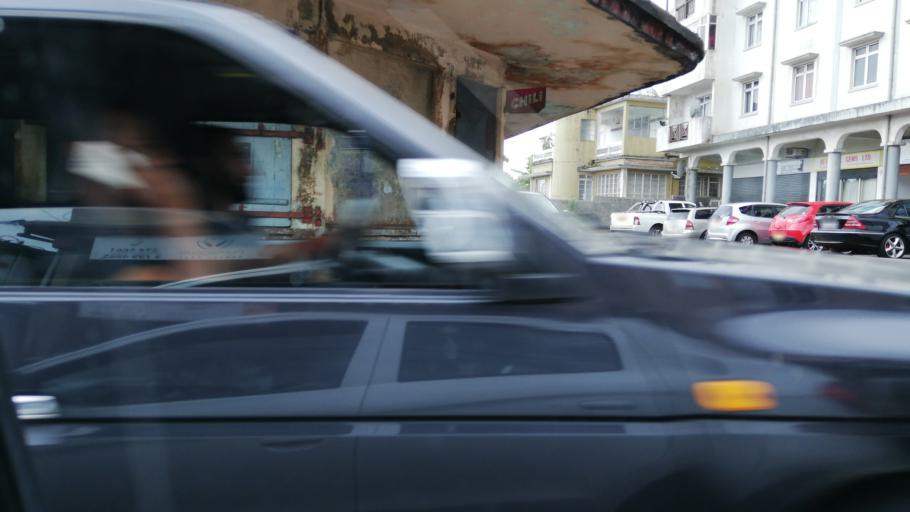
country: MU
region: Plaines Wilhems
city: Curepipe
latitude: -20.3164
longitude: 57.5280
